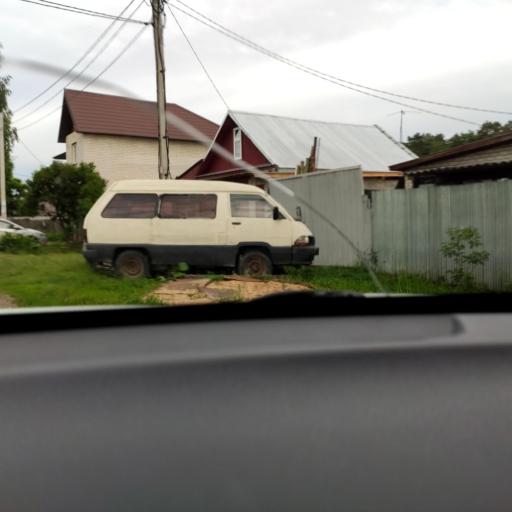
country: RU
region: Tatarstan
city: Osinovo
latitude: 55.8259
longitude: 48.8700
